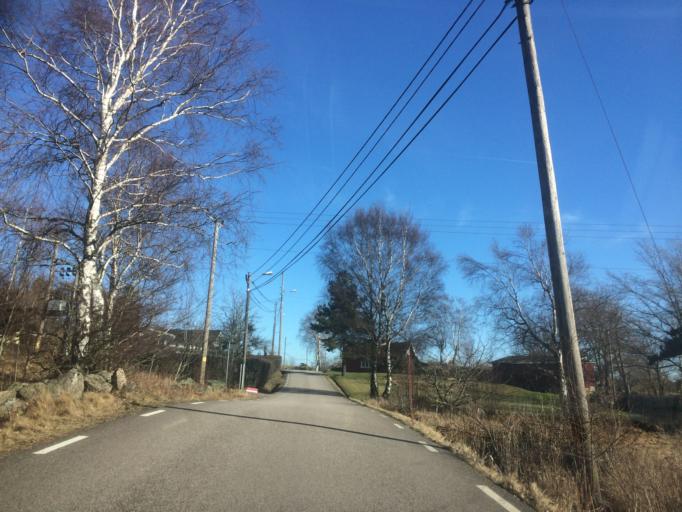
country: SE
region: Vaestra Goetaland
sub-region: Goteborg
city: Majorna
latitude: 57.7884
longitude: 11.8631
